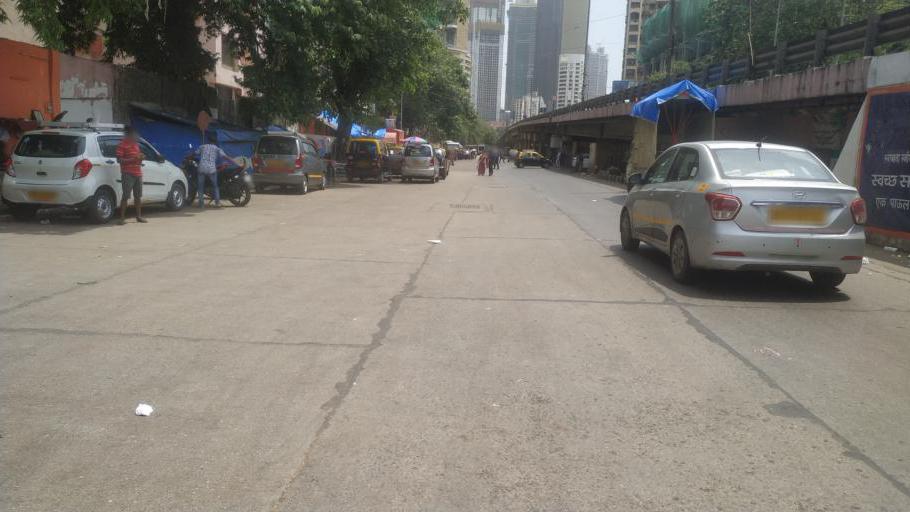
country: IN
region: Maharashtra
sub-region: Mumbai Suburban
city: Mumbai
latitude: 19.0114
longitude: 72.8357
